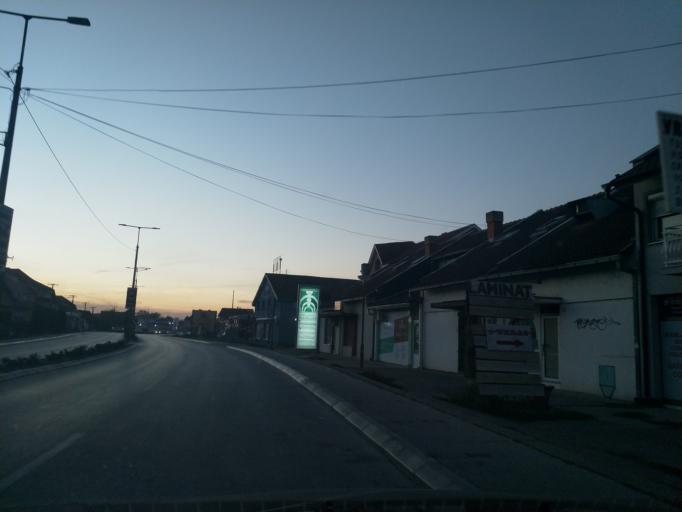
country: RS
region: Central Serbia
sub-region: Pomoravski Okrug
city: Svilajnac
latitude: 44.2326
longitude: 21.1899
